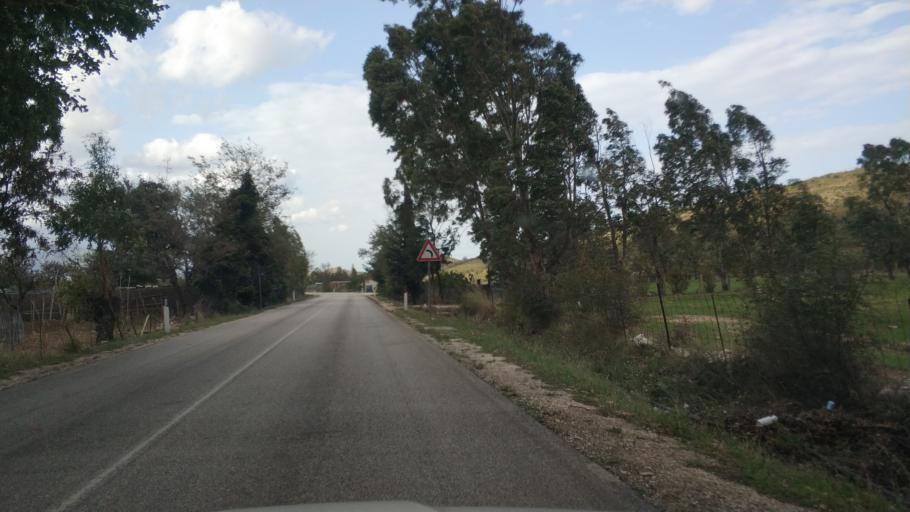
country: AL
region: Vlore
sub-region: Rrethi i Vlores
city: Orikum
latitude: 40.2794
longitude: 19.5030
